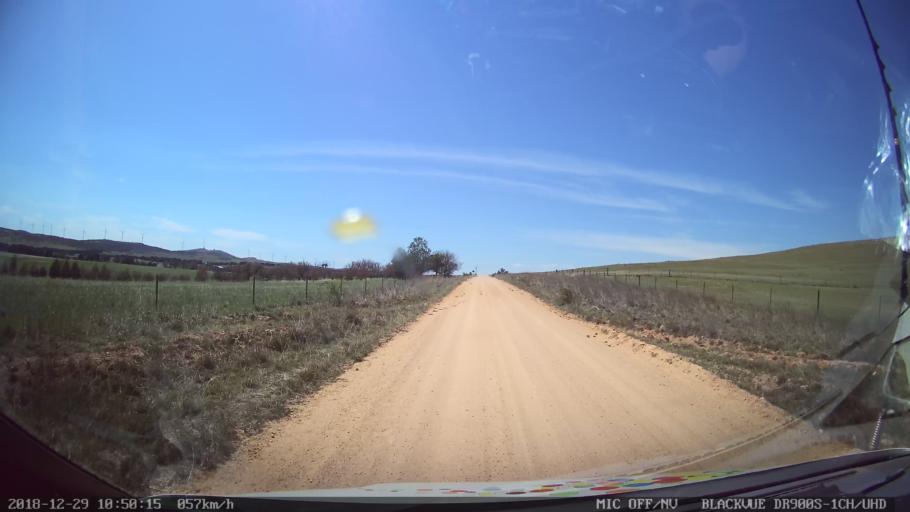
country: AU
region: New South Wales
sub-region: Palerang
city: Bungendore
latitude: -35.0807
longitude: 149.5213
